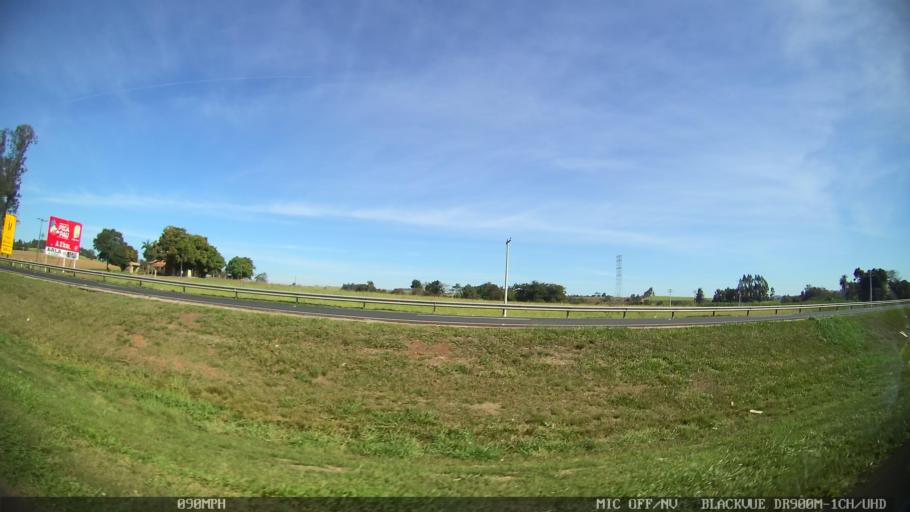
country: BR
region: Sao Paulo
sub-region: Pirassununga
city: Pirassununga
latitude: -22.0565
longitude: -47.4276
